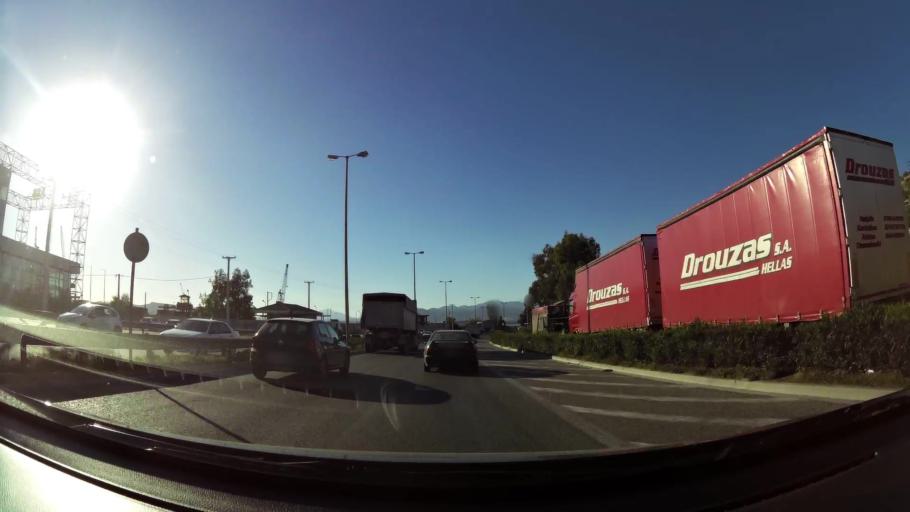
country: GR
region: Attica
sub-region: Nomarchia Athinas
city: Skaramangas
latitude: 38.0134
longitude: 23.6015
